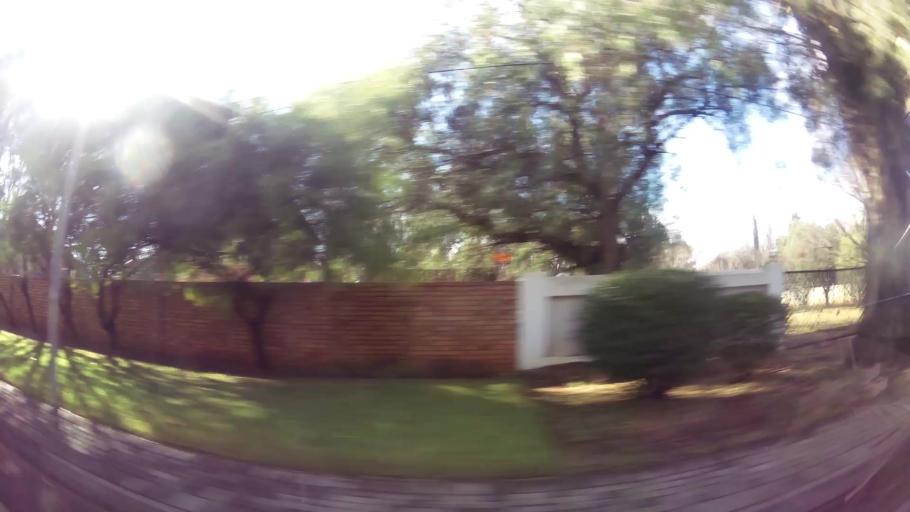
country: ZA
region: Gauteng
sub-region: Sedibeng District Municipality
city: Meyerton
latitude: -26.5387
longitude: 28.0625
